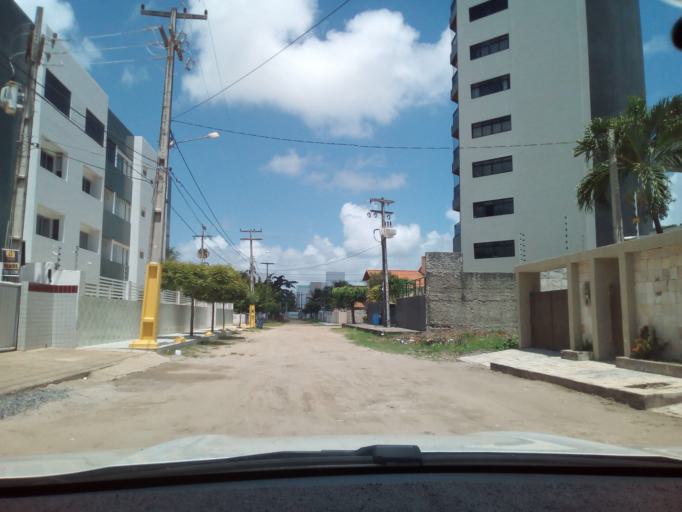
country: BR
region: Paraiba
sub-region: Cabedelo
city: Cabedelo
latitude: -7.0116
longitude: -34.8304
